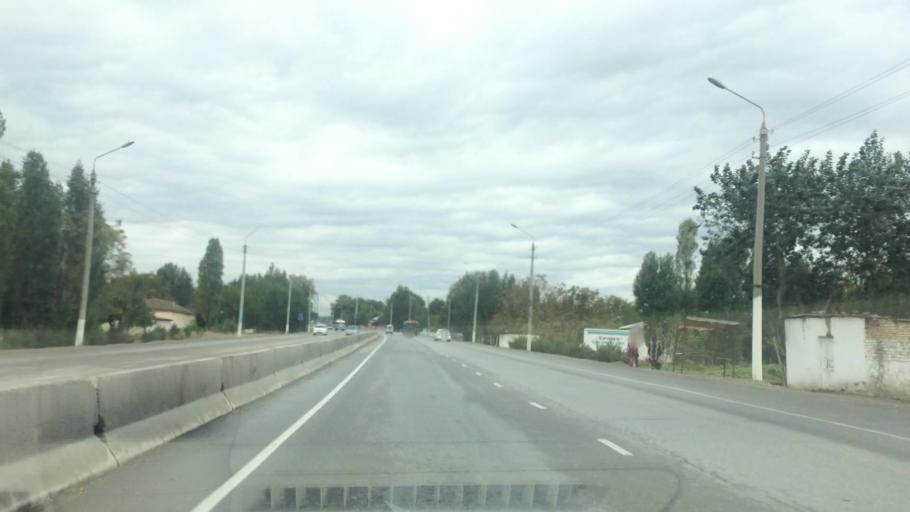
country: UZ
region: Jizzax
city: Jizzax
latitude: 39.9877
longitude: 67.5784
